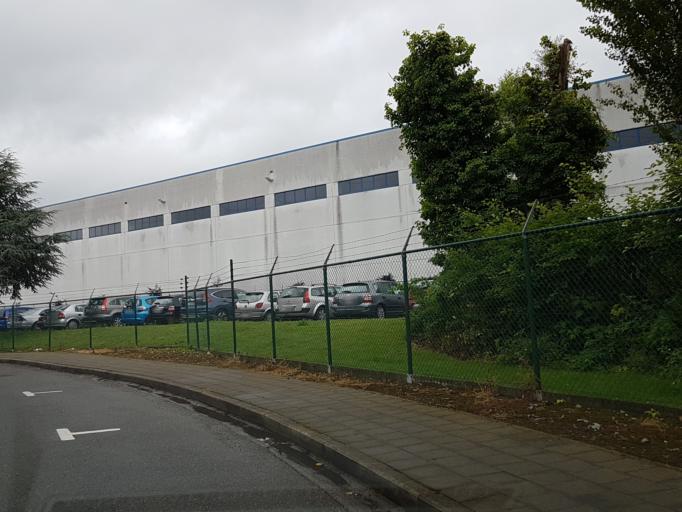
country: BE
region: Flanders
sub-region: Provincie Oost-Vlaanderen
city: Aalst
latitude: 50.9547
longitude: 4.0414
